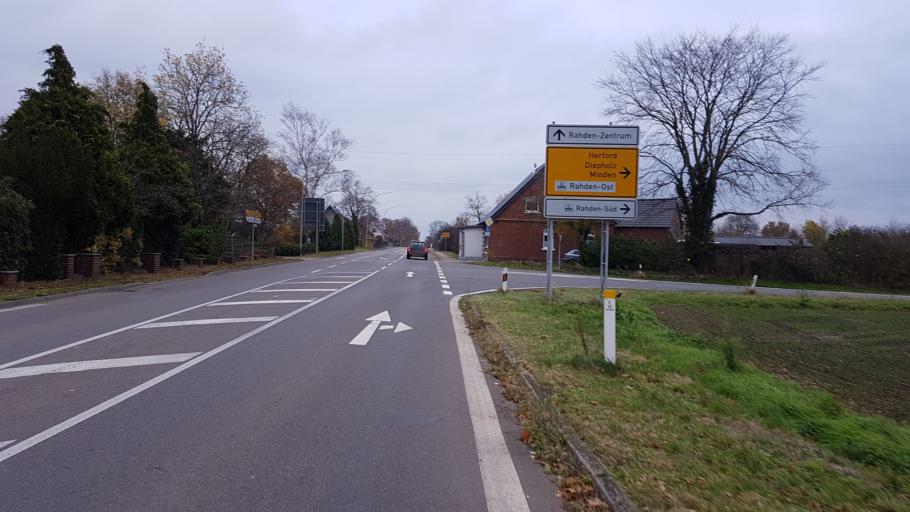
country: DE
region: North Rhine-Westphalia
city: Rahden
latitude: 52.4268
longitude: 8.6027
